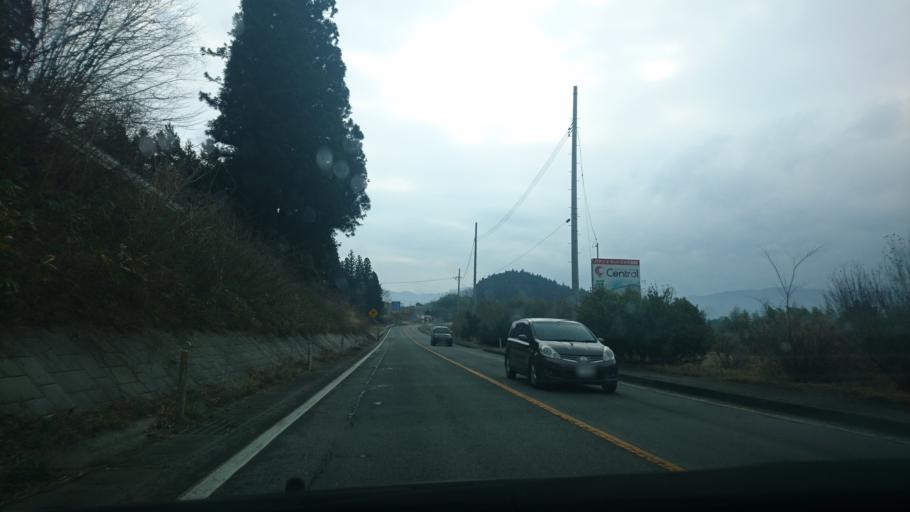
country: JP
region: Iwate
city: Ofunato
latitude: 39.0189
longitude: 141.6710
